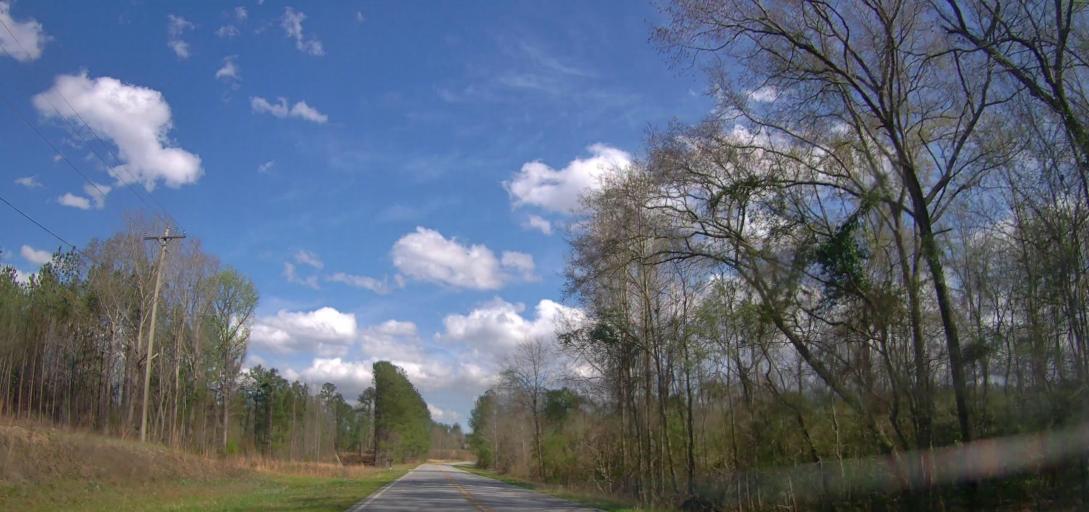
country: US
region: Georgia
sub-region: Wilkinson County
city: Gordon
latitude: 32.8258
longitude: -83.4154
